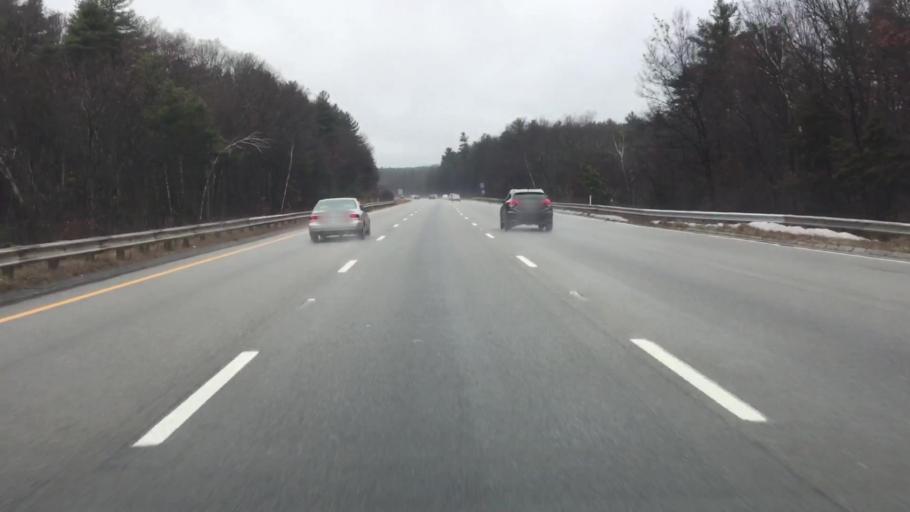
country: US
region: Massachusetts
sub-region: Middlesex County
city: Hopkinton
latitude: 42.2189
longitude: -71.5470
